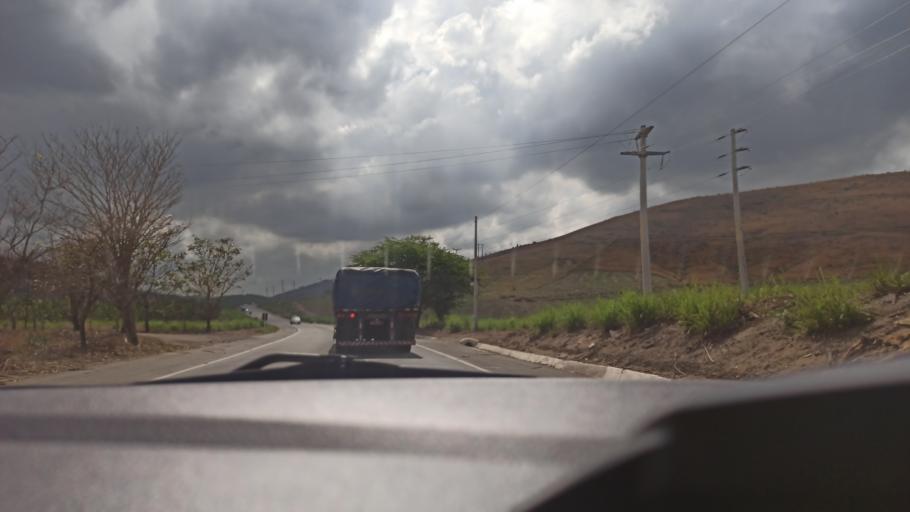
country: BR
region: Pernambuco
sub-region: Timbauba
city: Timbauba
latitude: -7.5224
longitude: -35.3008
